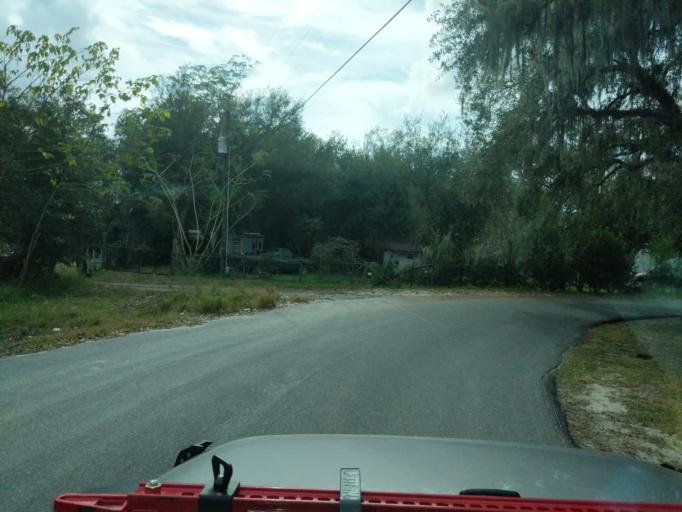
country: US
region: Florida
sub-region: Lake County
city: Mascotte
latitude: 28.5740
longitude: -81.9186
